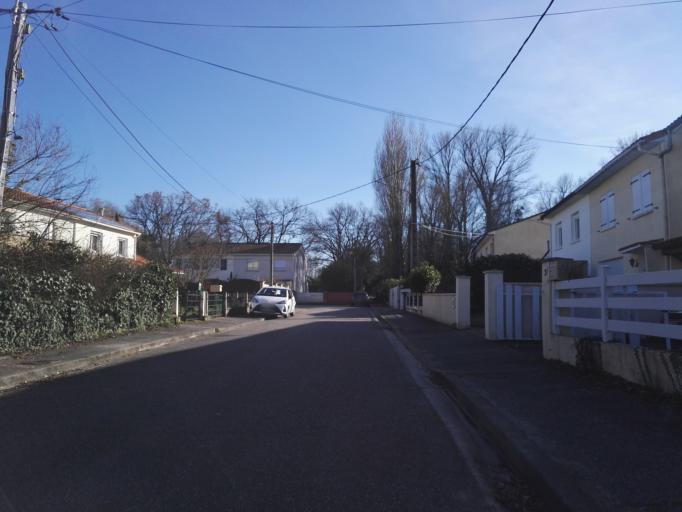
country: FR
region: Aquitaine
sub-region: Departement de la Gironde
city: Merignac
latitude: 44.8264
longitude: -0.6352
